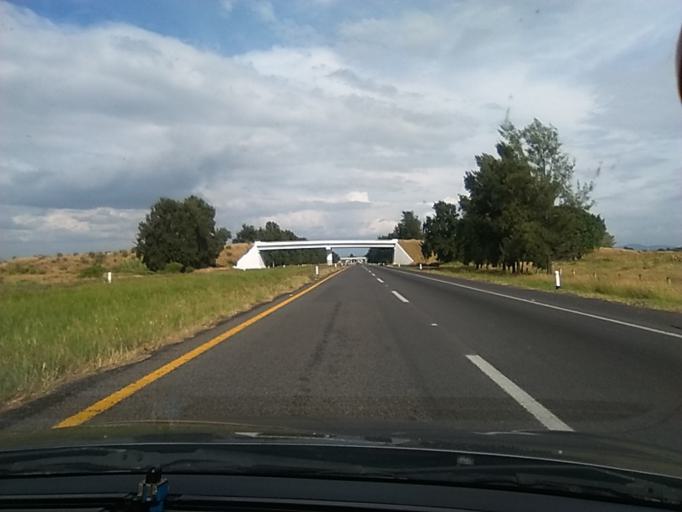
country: MX
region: Jalisco
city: La Barca
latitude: 20.3220
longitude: -102.5234
